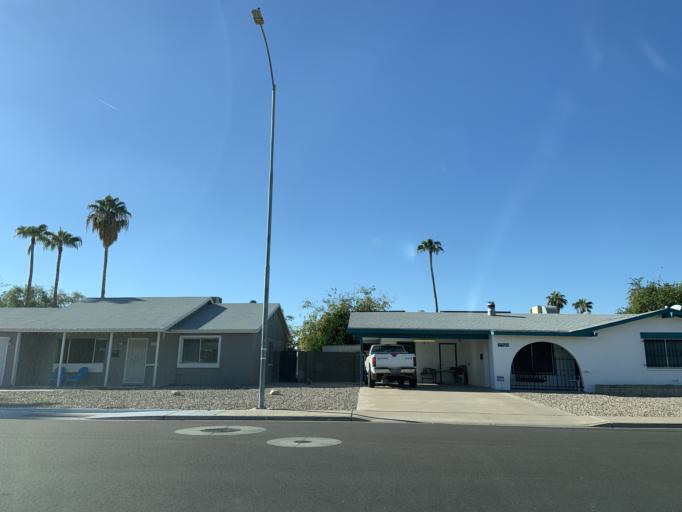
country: US
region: Arizona
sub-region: Maricopa County
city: Tempe
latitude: 33.4027
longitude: -111.8784
